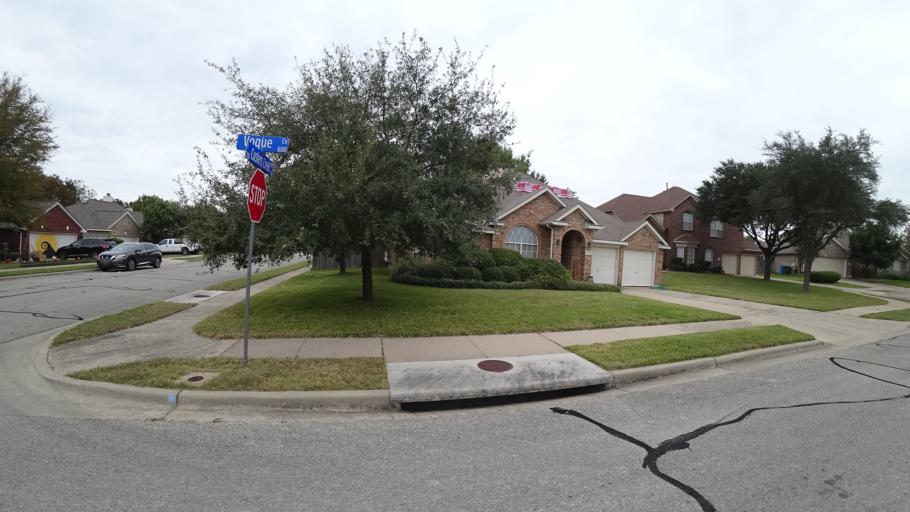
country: US
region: Texas
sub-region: Travis County
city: Pflugerville
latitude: 30.4331
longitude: -97.6235
